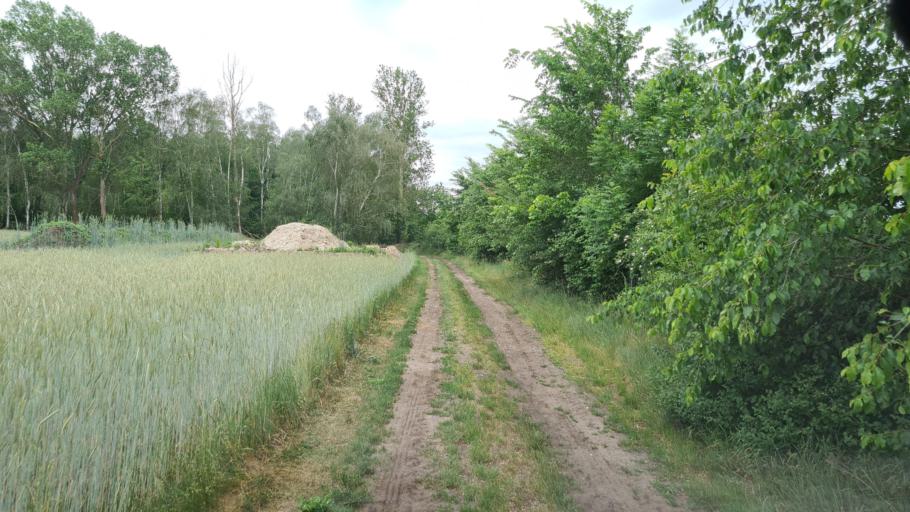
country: DE
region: Brandenburg
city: Bronkow
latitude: 51.6266
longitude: 13.9237
